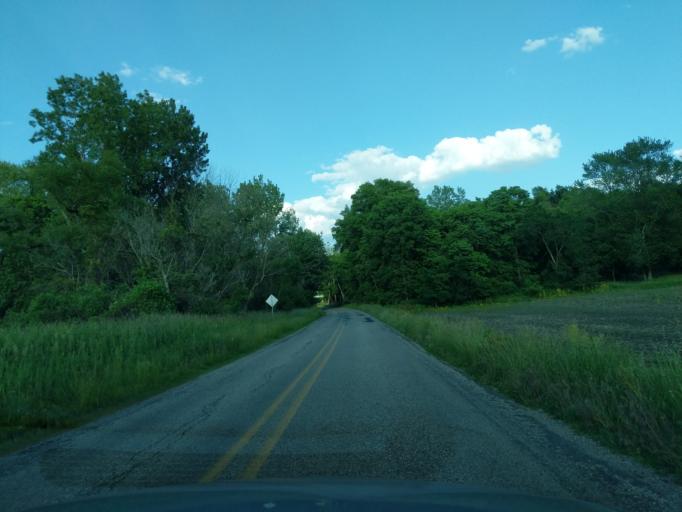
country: US
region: Indiana
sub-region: Whitley County
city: Tri-Lakes
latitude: 41.3025
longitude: -85.5540
